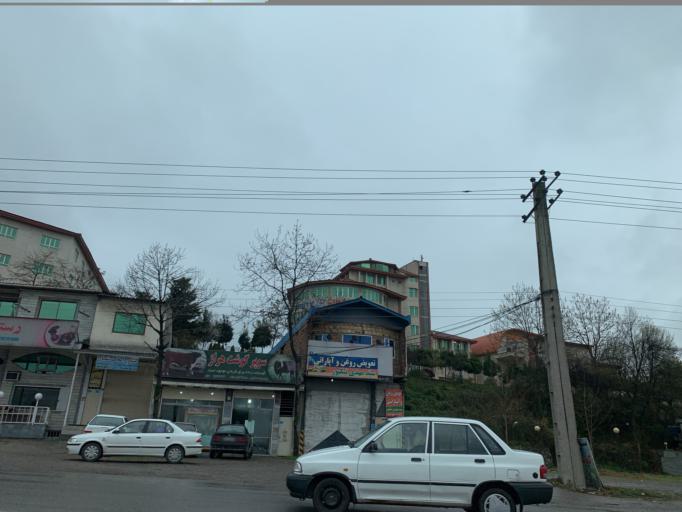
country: IR
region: Mazandaran
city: Amol
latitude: 36.4014
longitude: 52.3466
